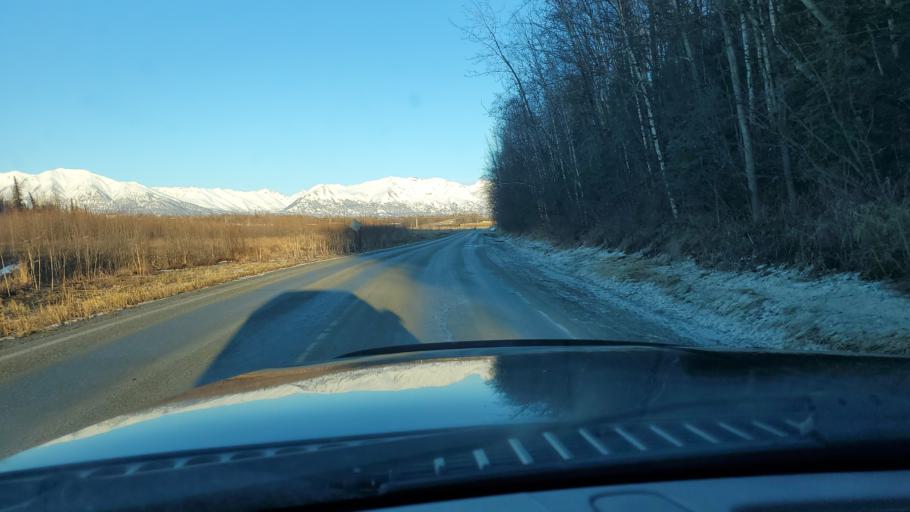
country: US
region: Alaska
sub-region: Matanuska-Susitna Borough
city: Gateway
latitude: 61.5923
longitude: -149.2457
